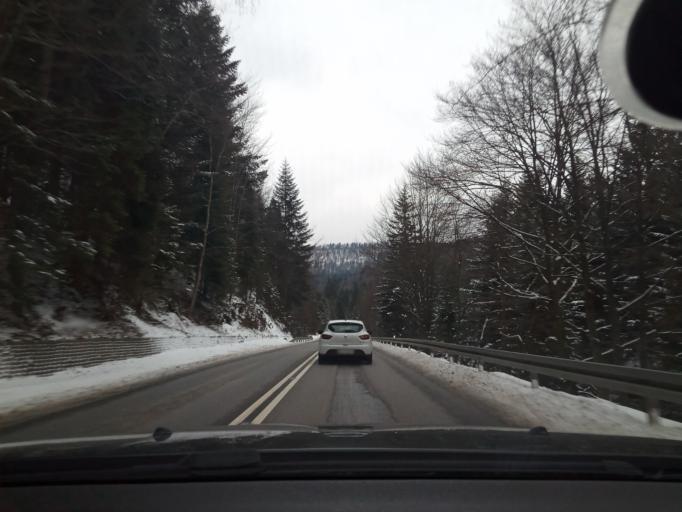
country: PL
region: Lesser Poland Voivodeship
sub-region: Powiat limanowski
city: Lubomierz
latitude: 49.6167
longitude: 20.2411
